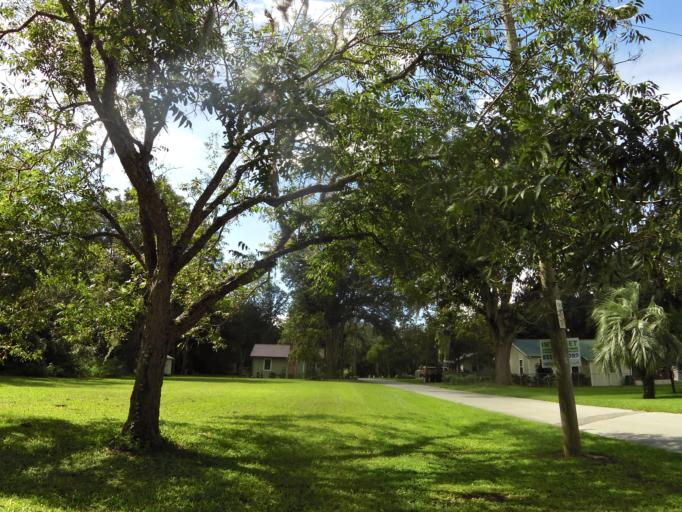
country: US
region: Florida
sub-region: Union County
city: Lake Butler
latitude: 30.0201
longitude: -82.3406
